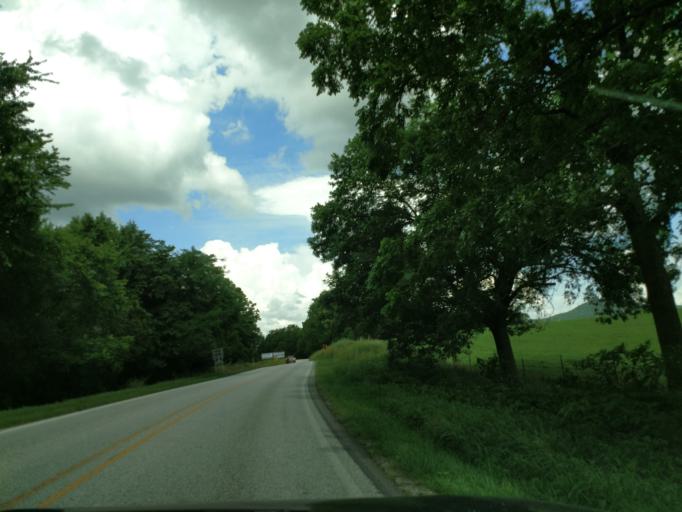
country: US
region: Arkansas
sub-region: Carroll County
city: Berryville
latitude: 36.4070
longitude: -93.5643
